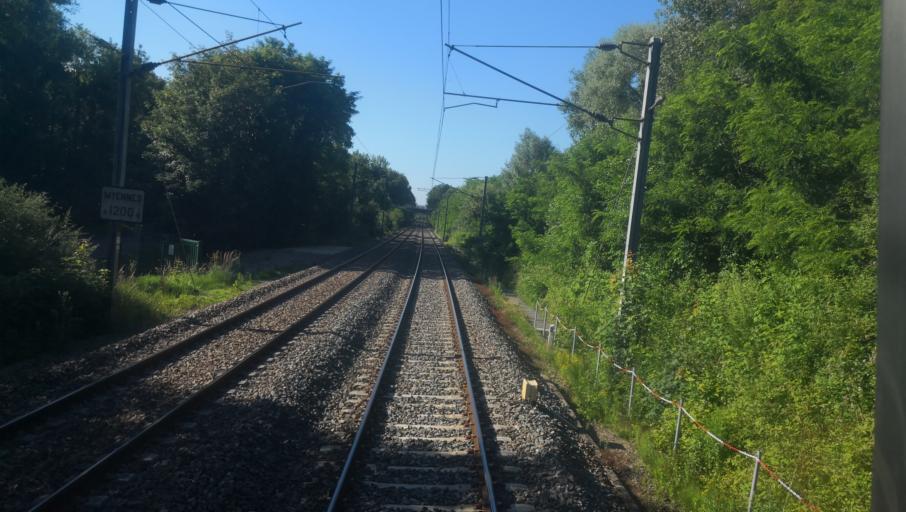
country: FR
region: Bourgogne
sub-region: Departement de la Nievre
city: Cosne-Cours-sur-Loire
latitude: 47.4387
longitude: 2.9337
